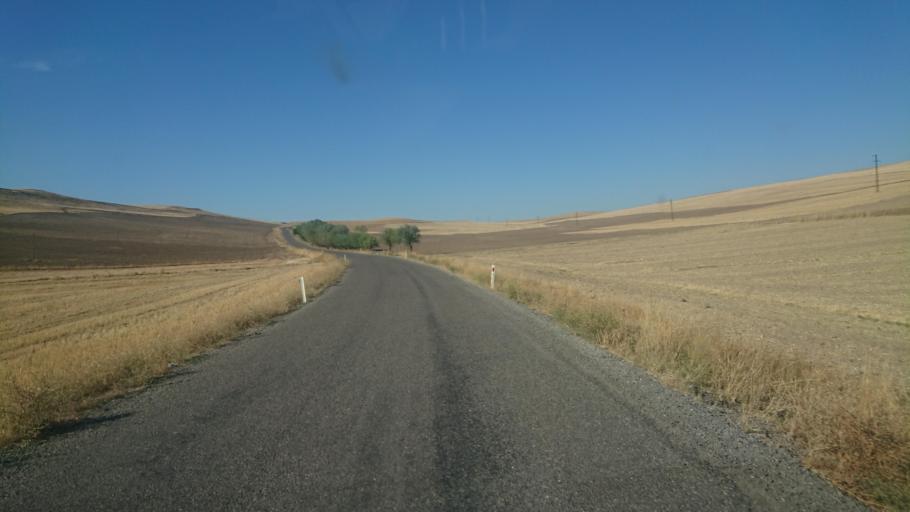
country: TR
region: Aksaray
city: Agacoren
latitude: 38.7987
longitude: 33.7146
